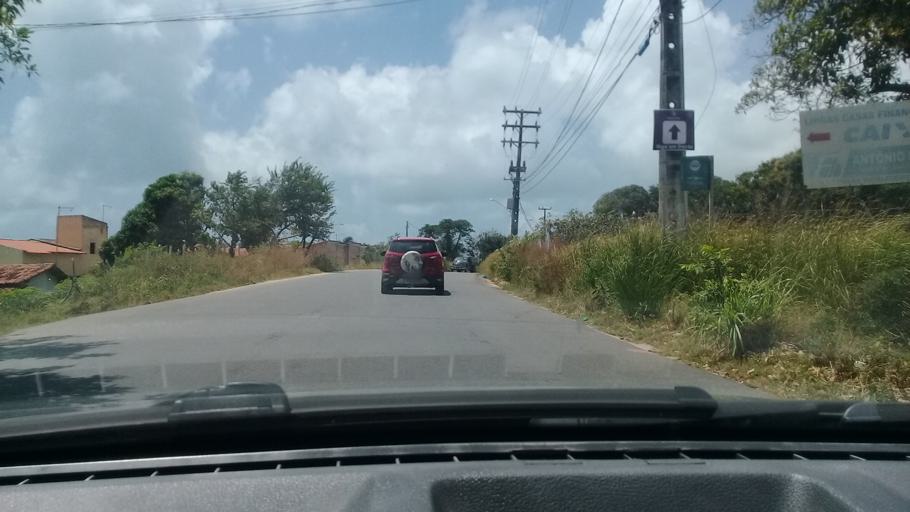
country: BR
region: Pernambuco
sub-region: Itamaraca
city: Itamaraca
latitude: -7.7758
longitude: -34.8362
